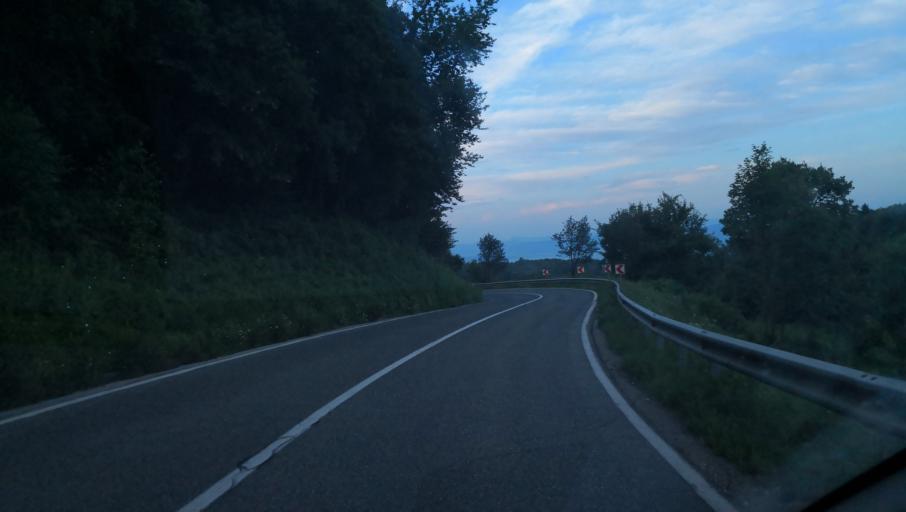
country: SI
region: Semic
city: Semic
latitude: 45.7144
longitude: 15.2324
